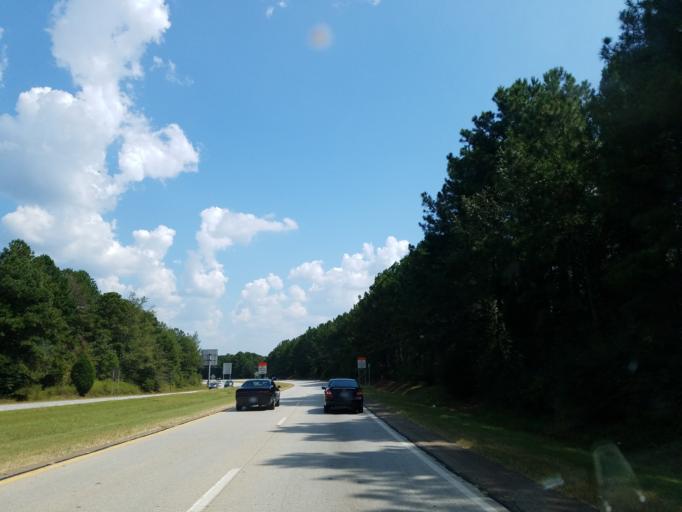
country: US
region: Georgia
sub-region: Oconee County
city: Watkinsville
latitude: 33.9099
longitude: -83.4413
